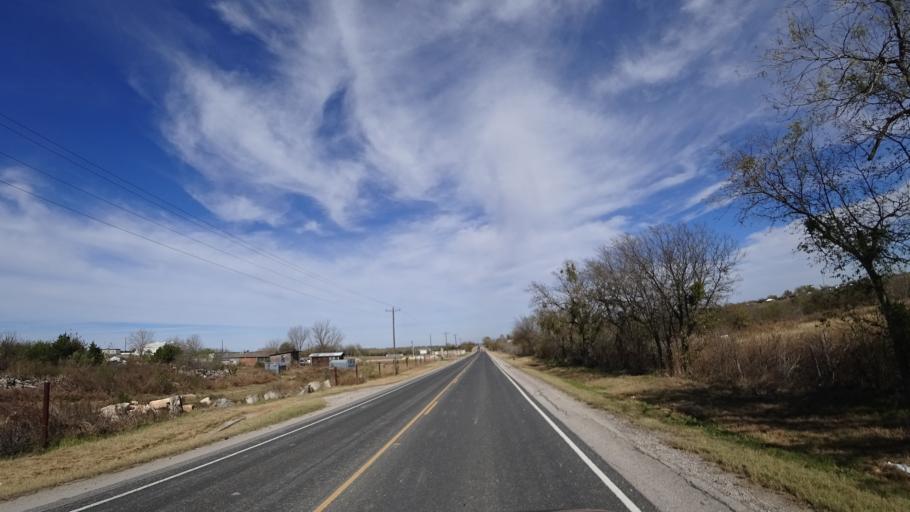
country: US
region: Texas
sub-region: Travis County
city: Onion Creek
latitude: 30.1023
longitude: -97.7268
